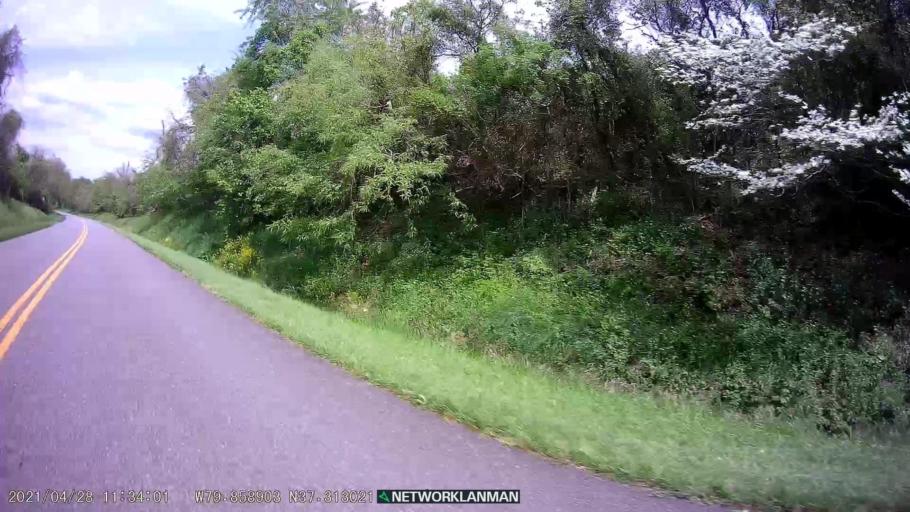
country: US
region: Virginia
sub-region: Roanoke County
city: Vinton
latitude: 37.3134
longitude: -79.8587
